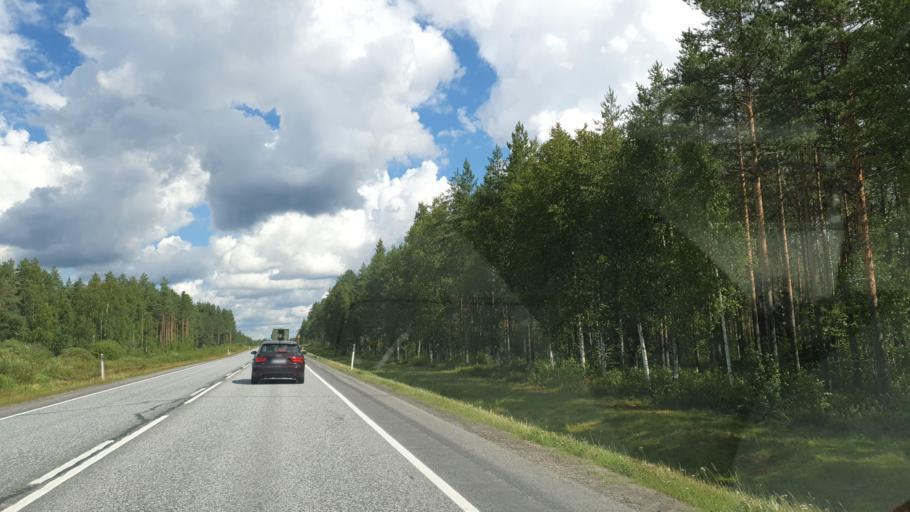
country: FI
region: Kainuu
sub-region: Kajaani
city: Kajaani
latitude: 64.1260
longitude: 27.4703
